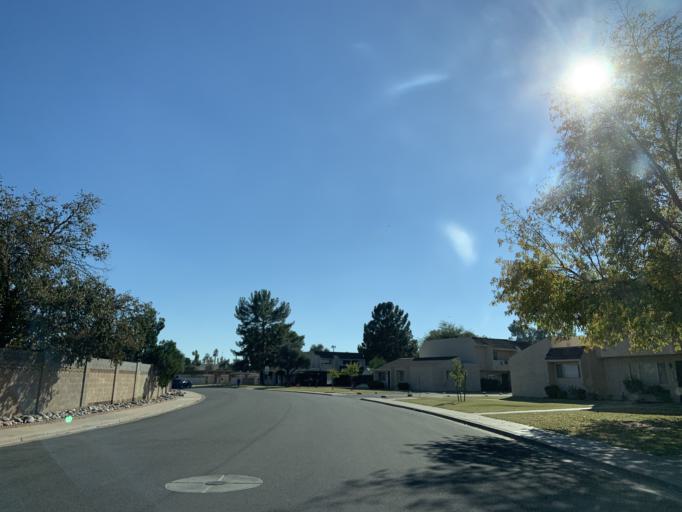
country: US
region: Arizona
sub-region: Maricopa County
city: Tempe
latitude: 33.3974
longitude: -111.8807
